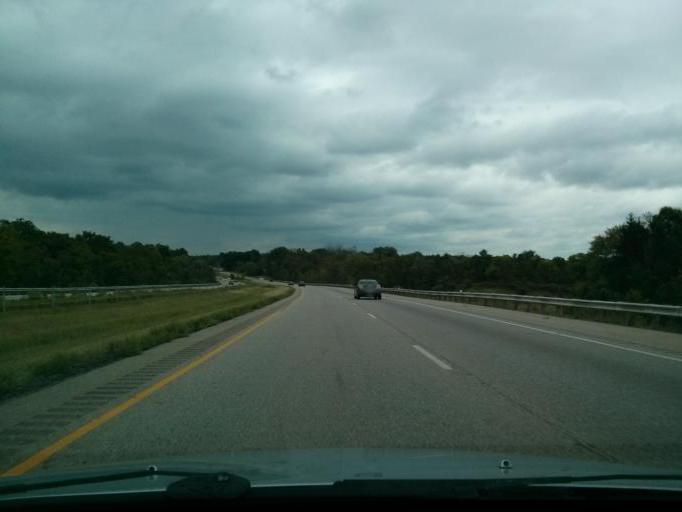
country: US
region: Ohio
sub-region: Mahoning County
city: Craig Beach
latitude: 41.1004
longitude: -81.0197
